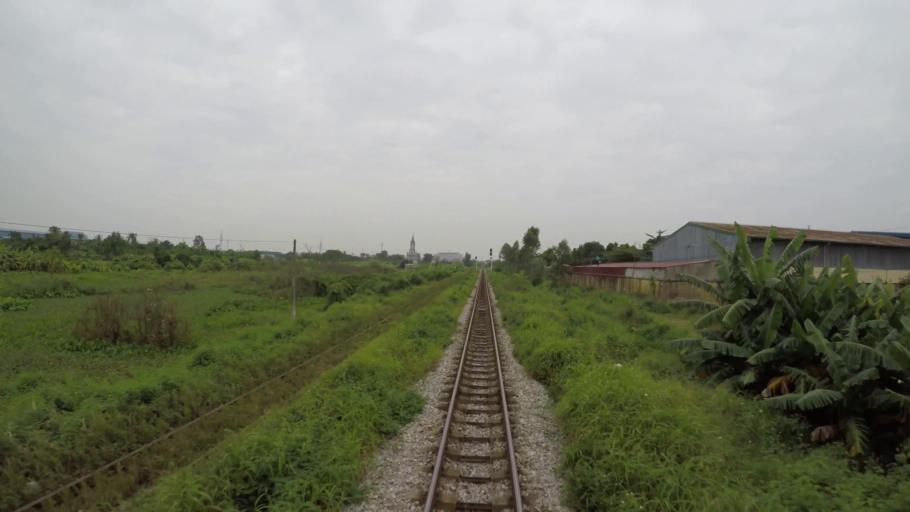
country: VN
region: Hai Phong
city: An Duong
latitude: 20.9035
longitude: 106.5762
